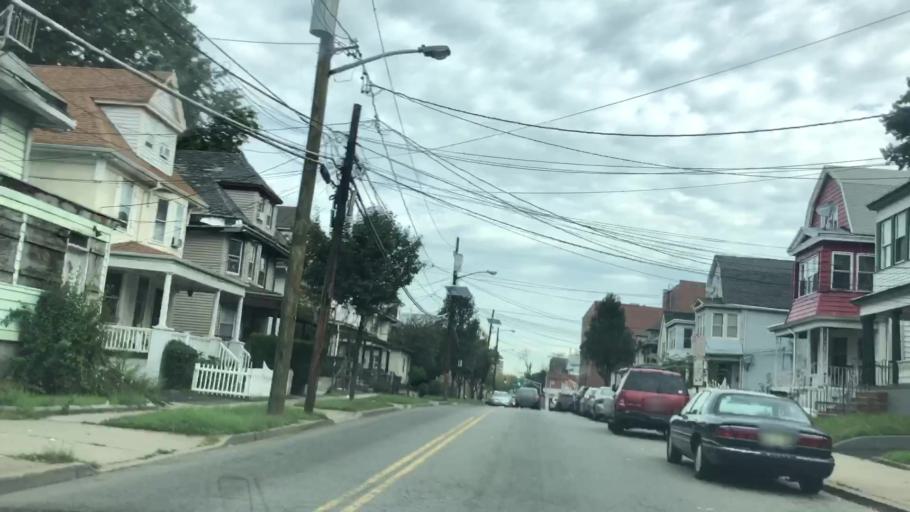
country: US
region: New Jersey
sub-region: Essex County
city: Irvington
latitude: 40.7234
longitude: -74.2237
